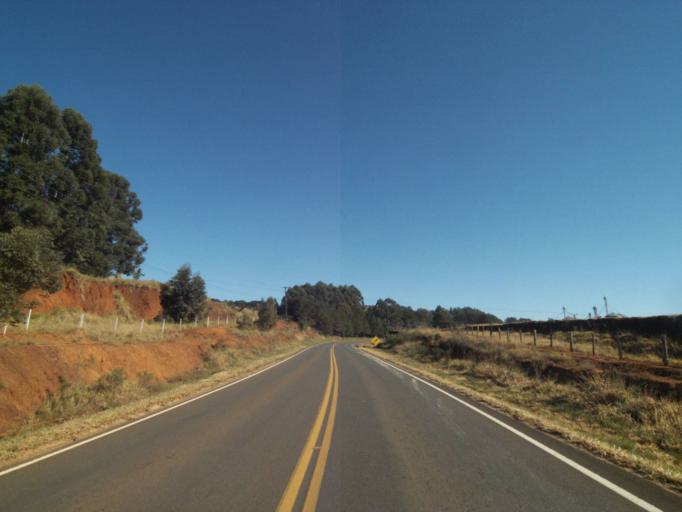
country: BR
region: Parana
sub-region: Tibagi
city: Tibagi
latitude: -24.5060
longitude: -50.4377
